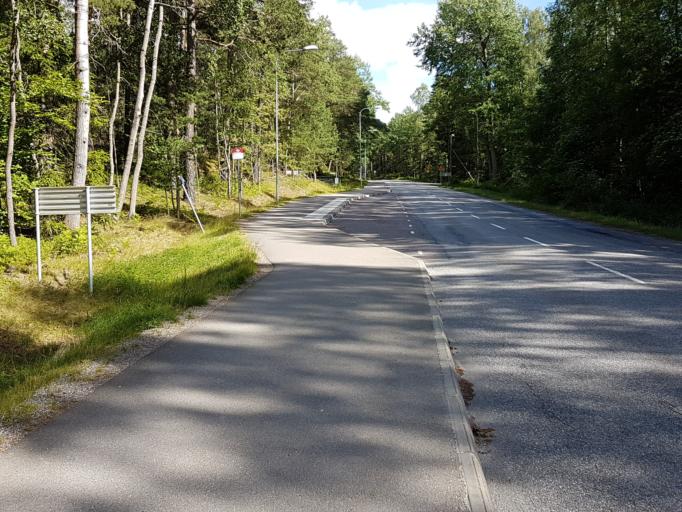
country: SE
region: Stockholm
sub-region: Nacka Kommun
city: Kummelnas
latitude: 59.3445
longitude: 18.2478
